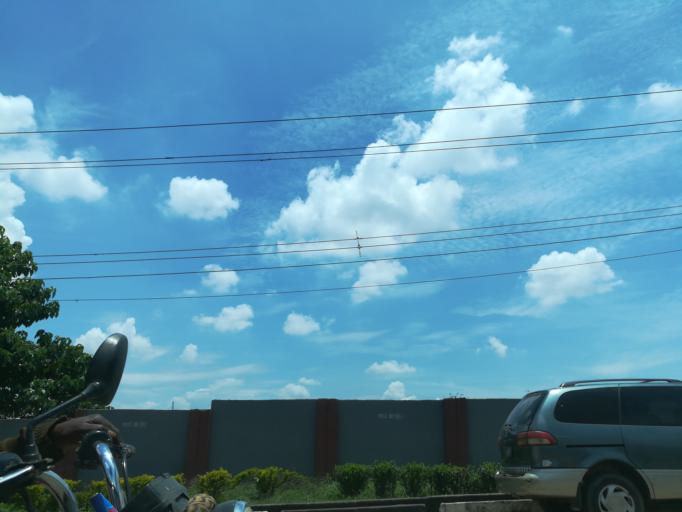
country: NG
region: Lagos
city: Ikorodu
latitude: 6.6105
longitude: 3.4998
